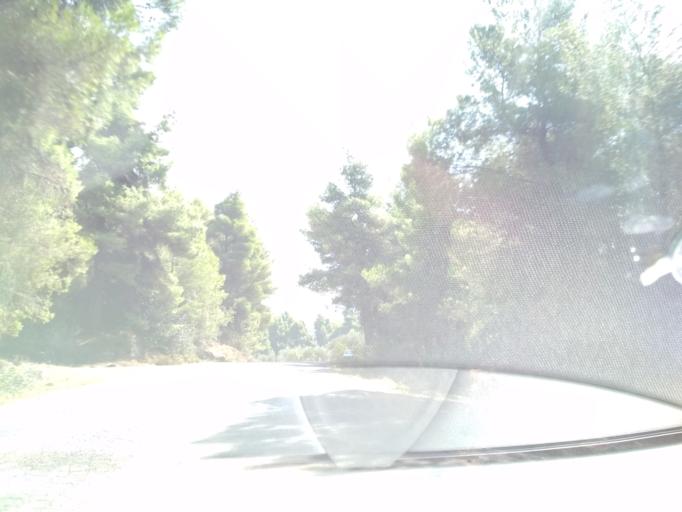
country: GR
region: Central Greece
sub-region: Nomos Evvoias
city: Roviai
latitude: 38.8257
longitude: 23.2557
